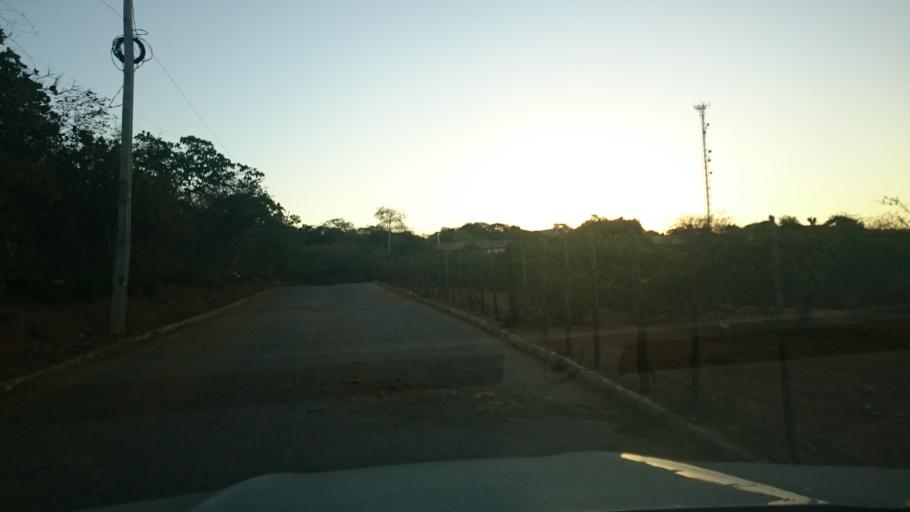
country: BR
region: Rio Grande do Norte
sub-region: Umarizal
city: Umarizal
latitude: -6.0221
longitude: -37.9961
